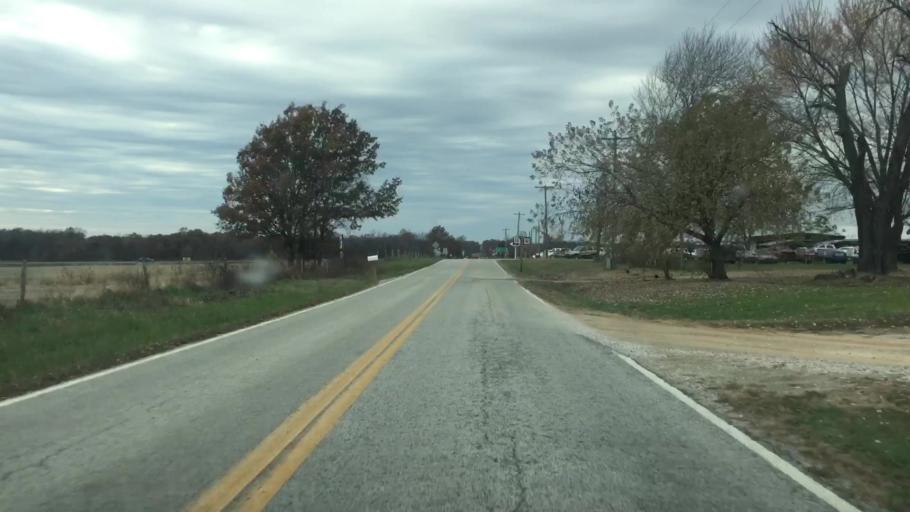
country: US
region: Missouri
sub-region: Saint Clair County
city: Osceola
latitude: 37.9899
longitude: -93.6481
